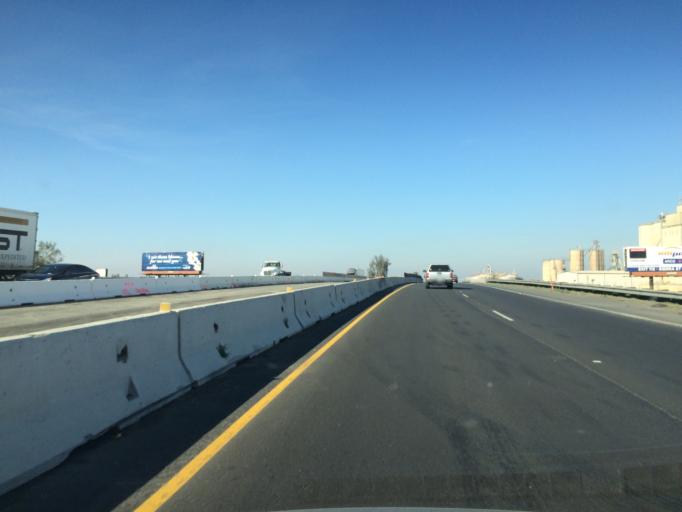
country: US
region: California
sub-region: Tulare County
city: Goshen
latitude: 36.3541
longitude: -119.4280
